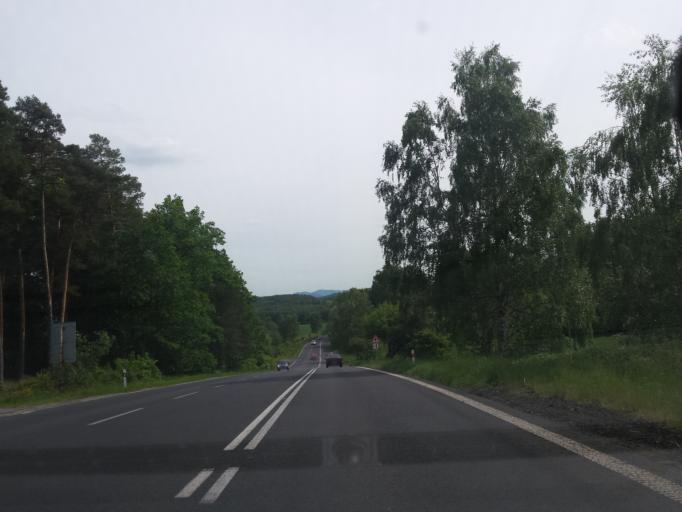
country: CZ
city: Novy Bor
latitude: 50.7428
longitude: 14.5511
